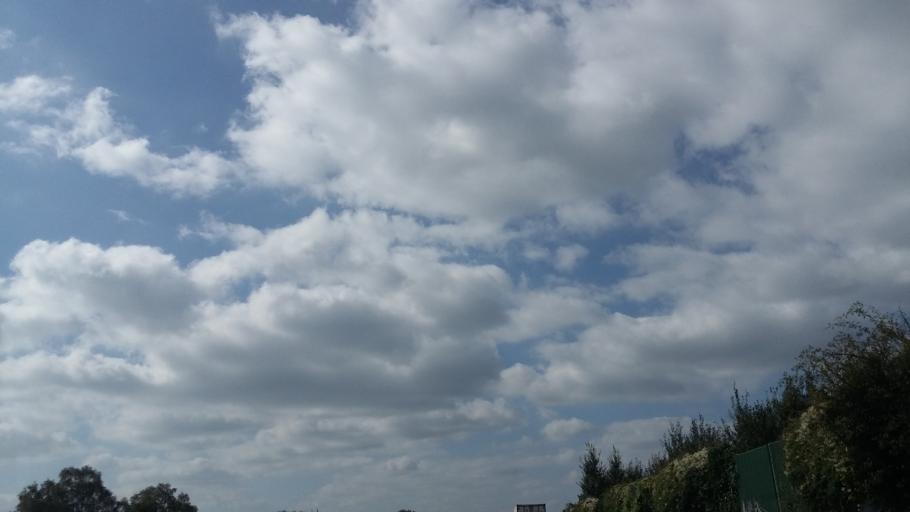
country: DE
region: Lower Saxony
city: Ritterhude
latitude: 53.1304
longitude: 8.7621
